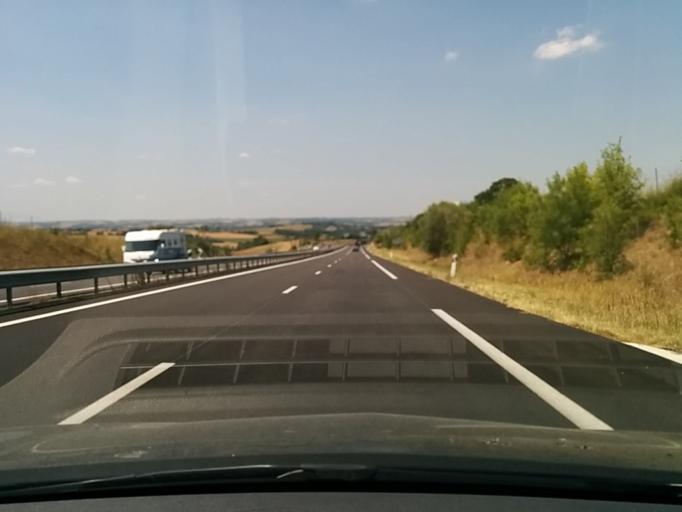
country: FR
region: Midi-Pyrenees
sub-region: Departement du Gers
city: Pujaudran
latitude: 43.5952
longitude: 1.1191
